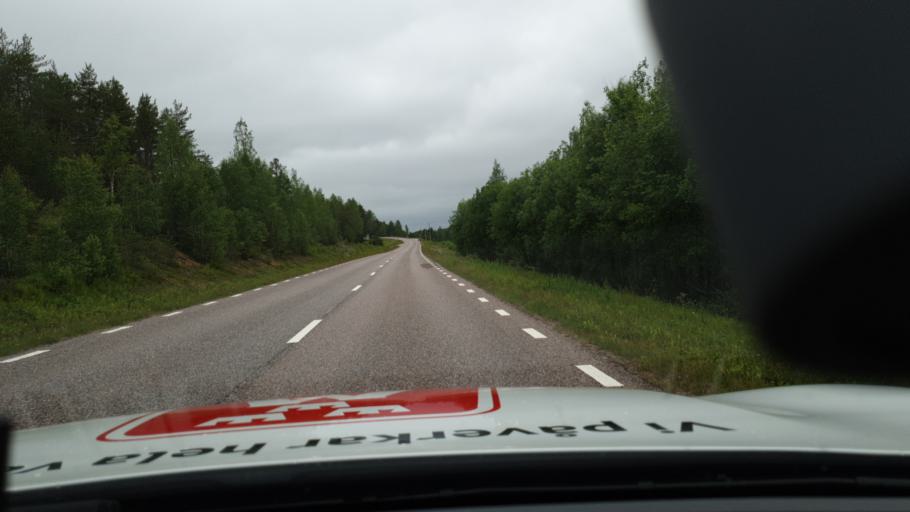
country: FI
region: Lapland
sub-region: Tunturi-Lappi
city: Kolari
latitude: 67.0274
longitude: 23.7194
